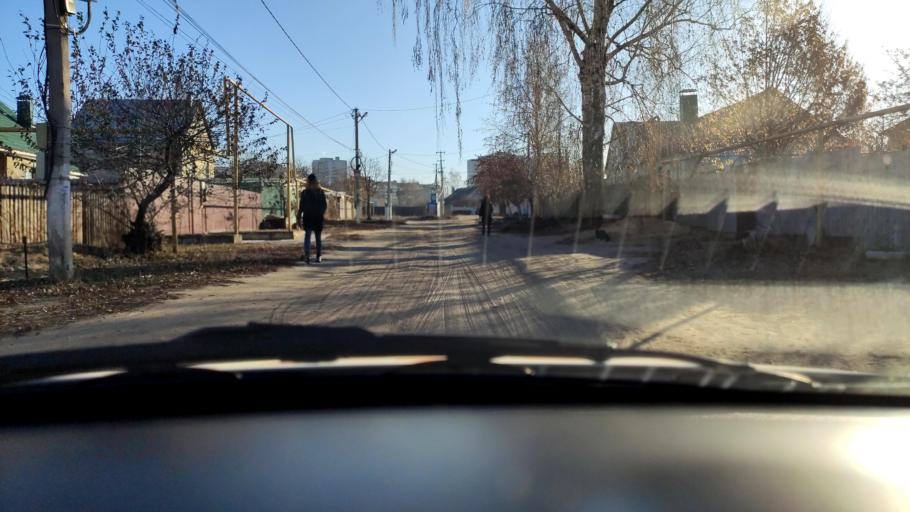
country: RU
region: Voronezj
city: Podgornoye
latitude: 51.7292
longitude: 39.1570
